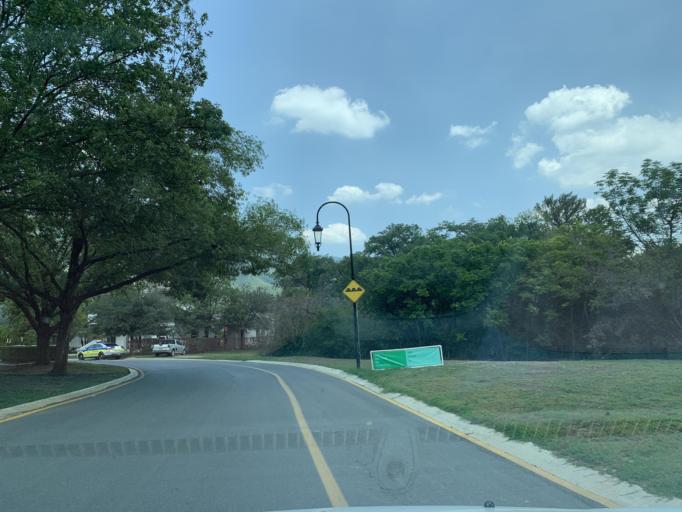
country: MX
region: Nuevo Leon
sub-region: Juarez
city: Bosques de San Pedro
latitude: 25.5166
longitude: -100.1973
